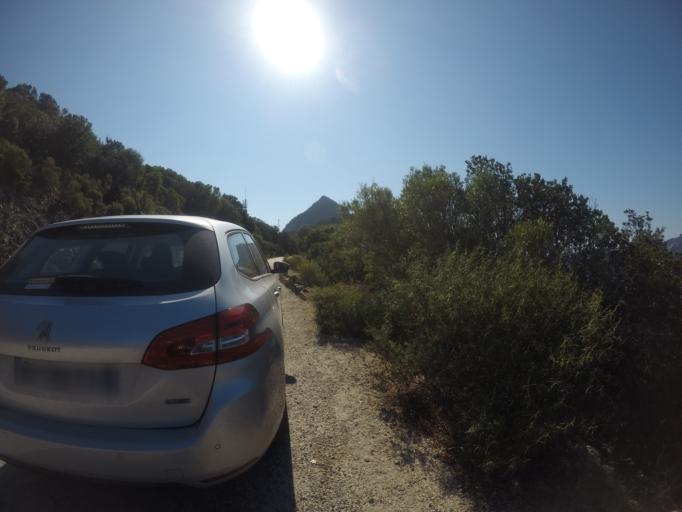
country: FR
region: Corsica
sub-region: Departement de la Corse-du-Sud
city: Cargese
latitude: 42.3274
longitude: 8.6338
